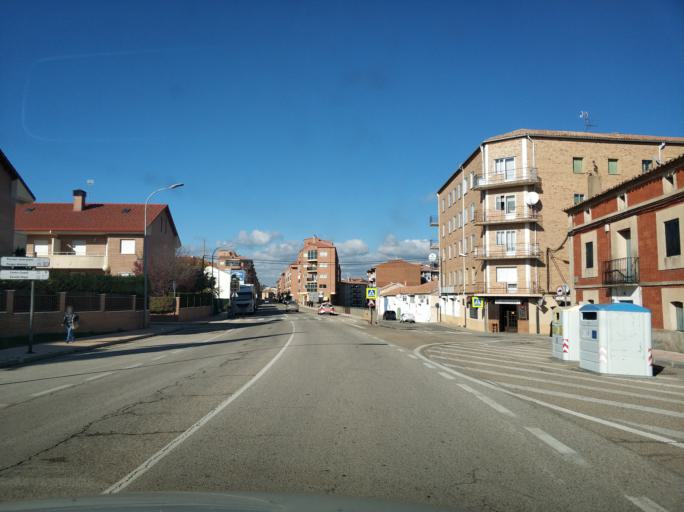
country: ES
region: Castille and Leon
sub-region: Provincia de Soria
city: Almazan
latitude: 41.4812
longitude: -2.5288
